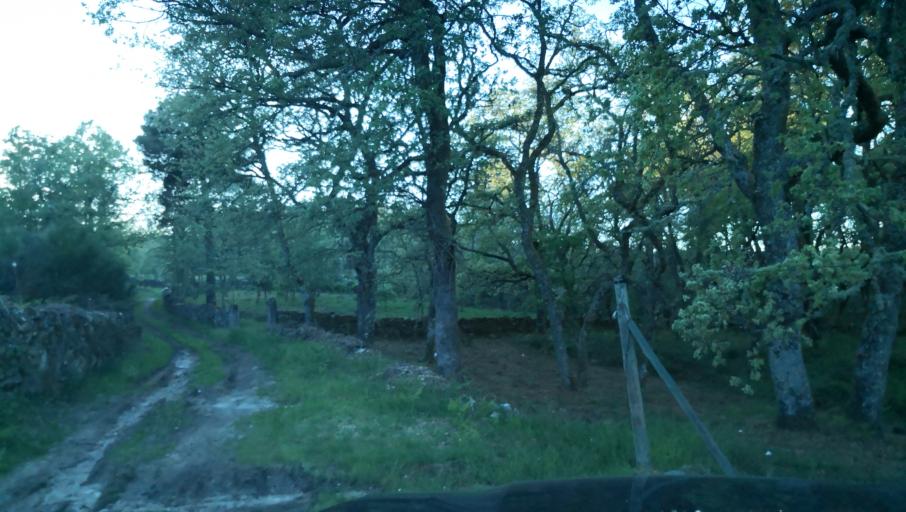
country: PT
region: Vila Real
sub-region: Sabrosa
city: Sabrosa
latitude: 41.3496
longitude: -7.6231
